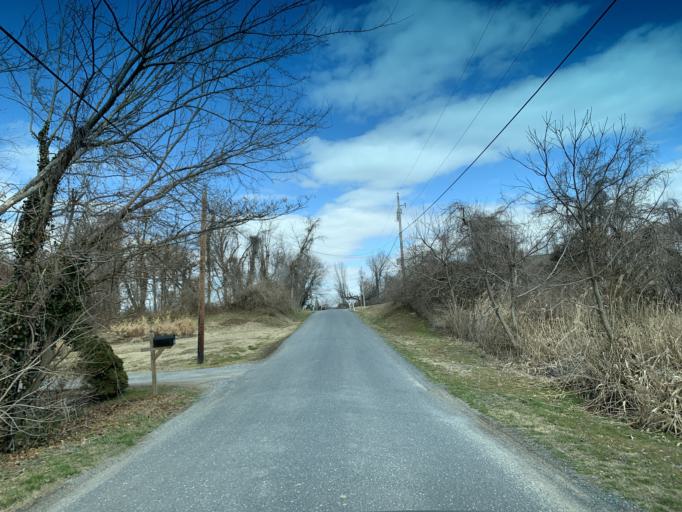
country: US
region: Maryland
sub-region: Queen Anne's County
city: Stevensville
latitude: 39.0351
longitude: -76.3090
